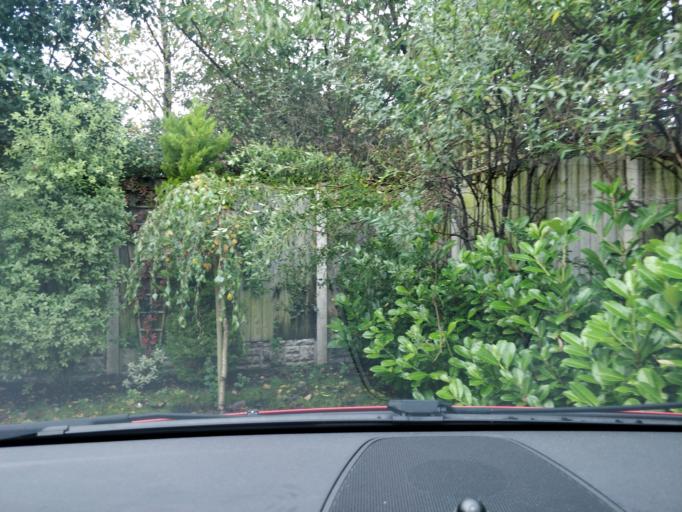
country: GB
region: England
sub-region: Sefton
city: Southport
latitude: 53.6296
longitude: -3.0102
